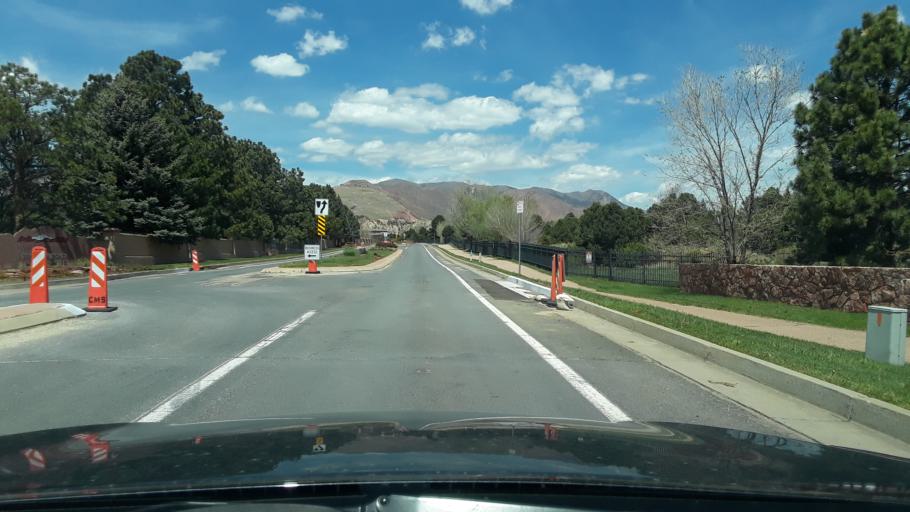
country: US
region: Colorado
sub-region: El Paso County
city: Manitou Springs
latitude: 38.8795
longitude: -104.8672
